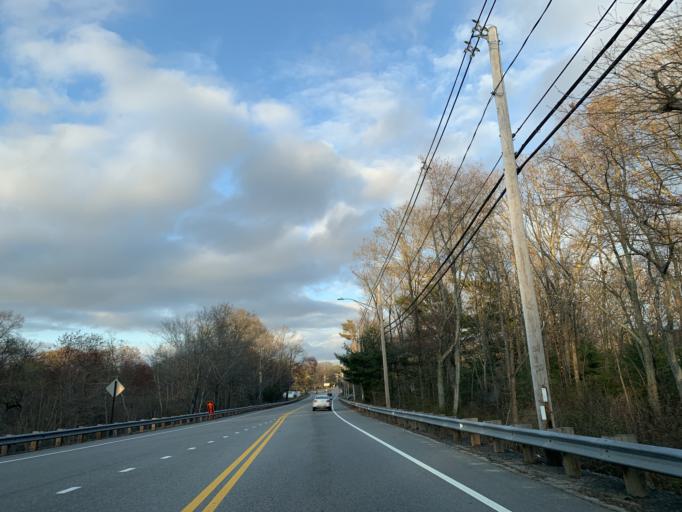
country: US
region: Massachusetts
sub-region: Bristol County
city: Attleboro
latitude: 41.9330
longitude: -71.3264
